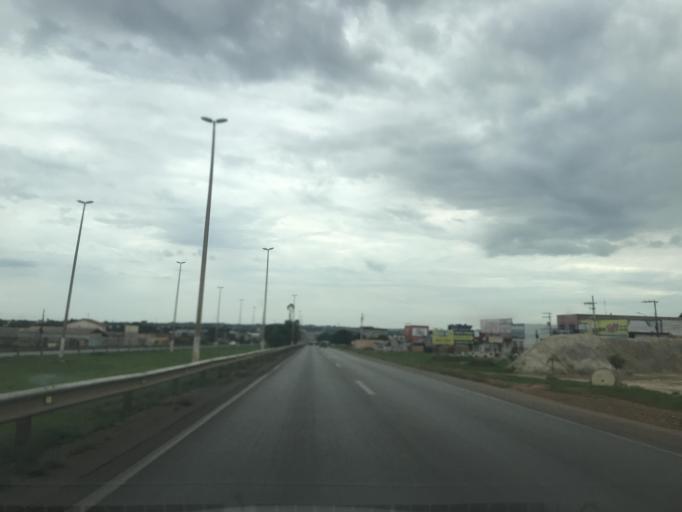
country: BR
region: Goias
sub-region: Luziania
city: Luziania
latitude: -16.1397
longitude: -47.9504
